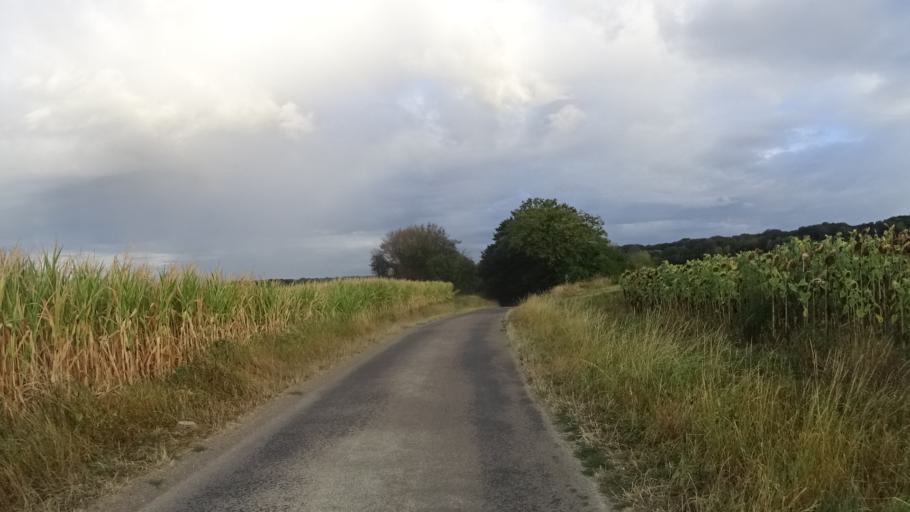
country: FR
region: Bourgogne
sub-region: Departement de Saone-et-Loire
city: Verdun-sur-le-Doubs
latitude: 46.9537
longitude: 5.0585
